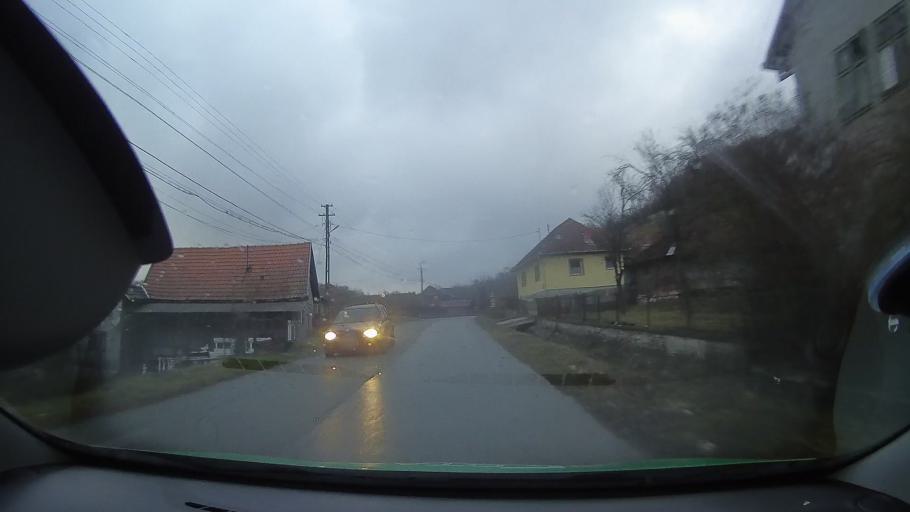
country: RO
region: Hunedoara
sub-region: Comuna Baia de Cris
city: Baia de Cris
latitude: 46.2125
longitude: 22.7142
